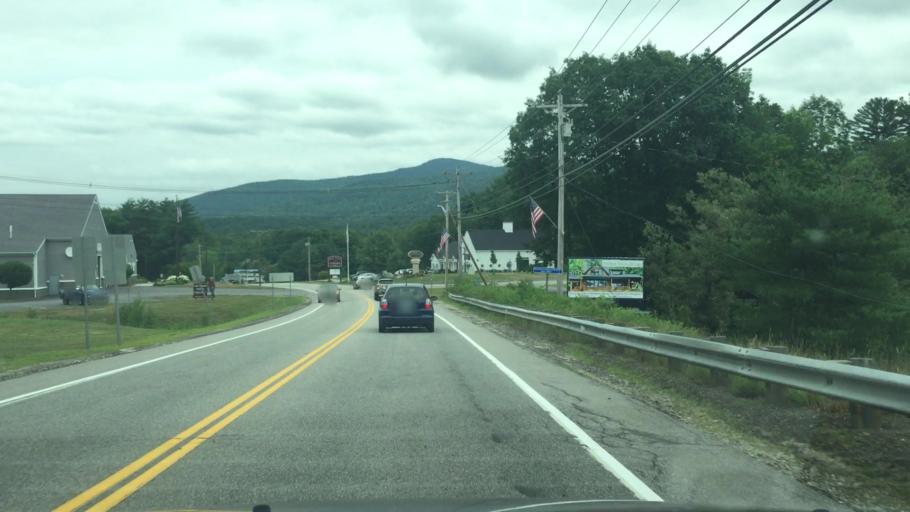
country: US
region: New Hampshire
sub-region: Carroll County
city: Moultonborough
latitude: 43.7555
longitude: -71.3951
